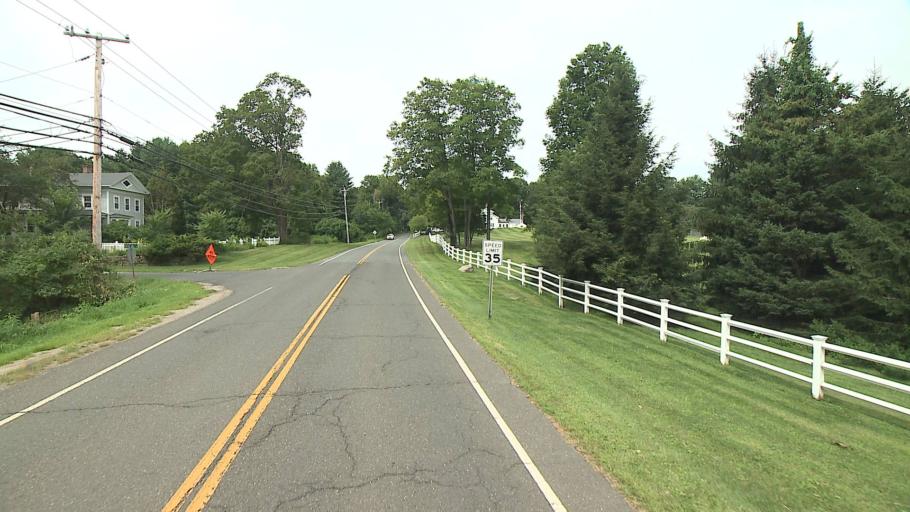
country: US
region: Connecticut
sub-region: Litchfield County
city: Woodbury
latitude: 41.5406
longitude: -73.2169
